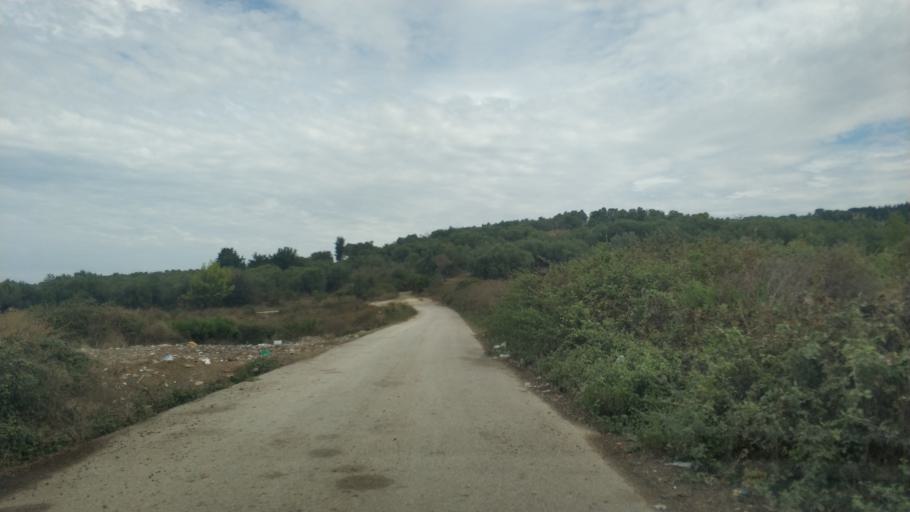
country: AL
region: Vlore
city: Vlore
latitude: 40.5116
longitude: 19.4104
